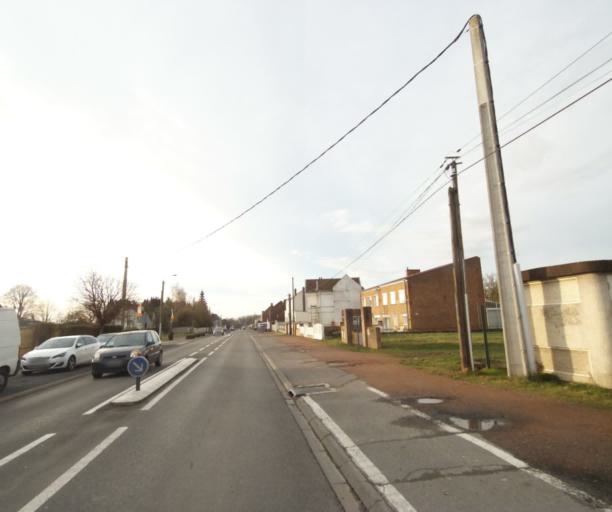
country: FR
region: Nord-Pas-de-Calais
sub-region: Departement du Nord
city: Conde-sur-l'Escaut
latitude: 50.4660
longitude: 3.5953
